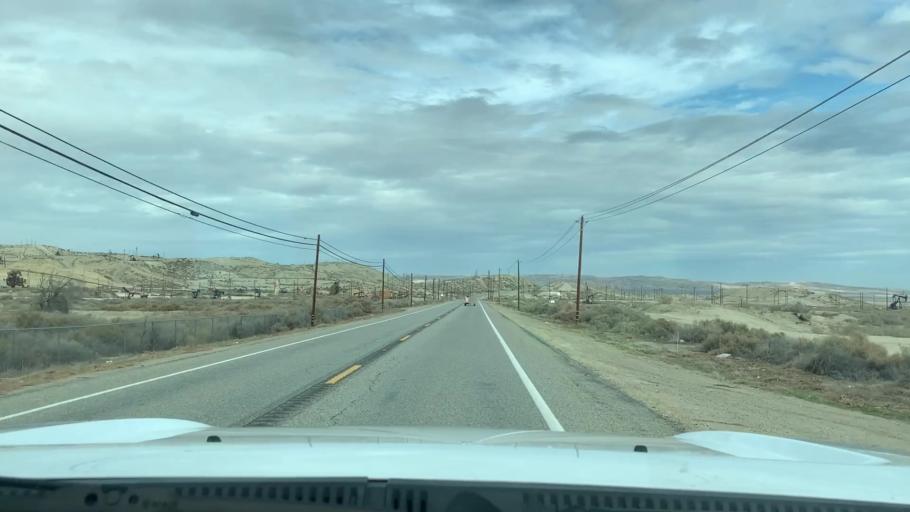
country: US
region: California
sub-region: Kern County
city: Maricopa
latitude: 35.0713
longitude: -119.4020
